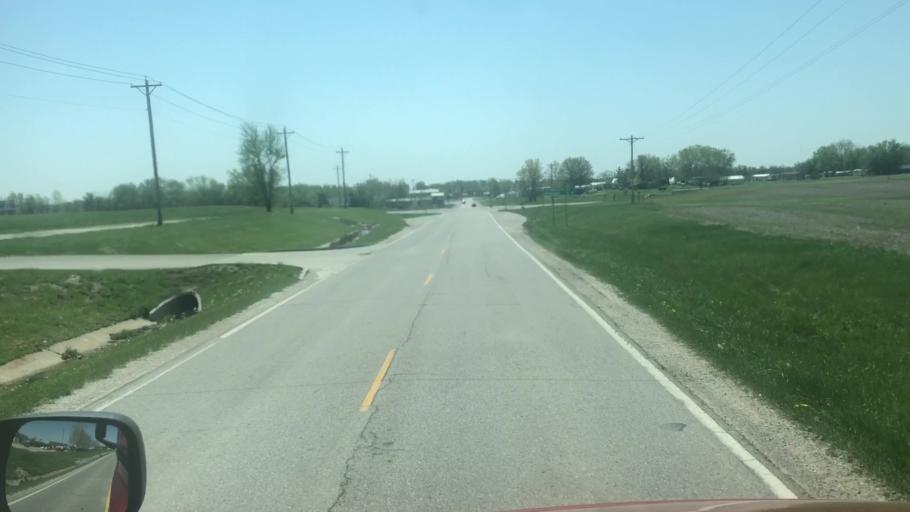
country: US
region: Missouri
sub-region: Adair County
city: Kirksville
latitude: 40.2186
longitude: -92.5923
